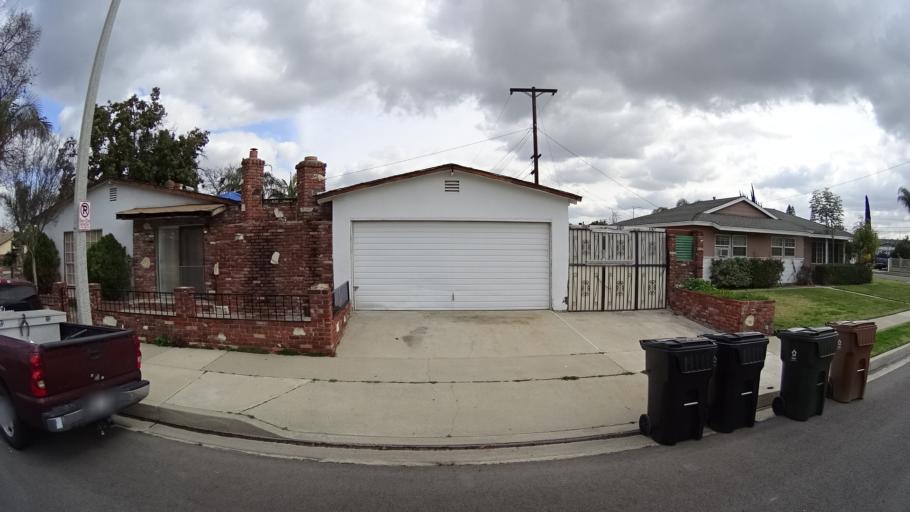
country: US
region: California
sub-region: Orange County
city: Buena Park
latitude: 33.8428
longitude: -117.9751
